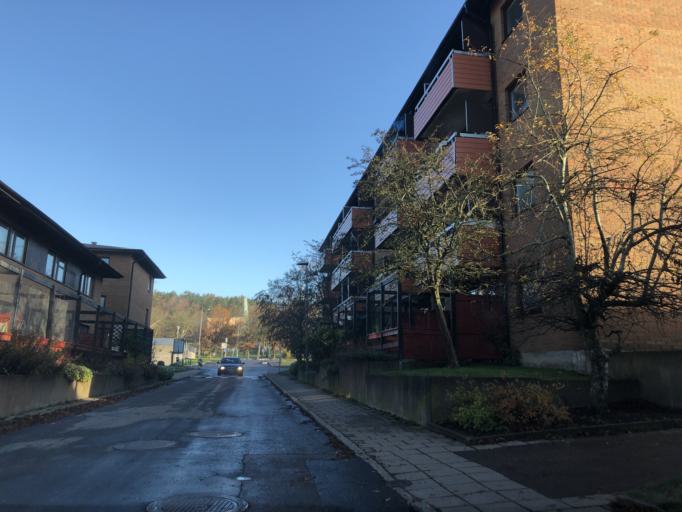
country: SE
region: Vaestra Goetaland
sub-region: Goteborg
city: Rannebergen
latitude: 57.7981
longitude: 12.0559
